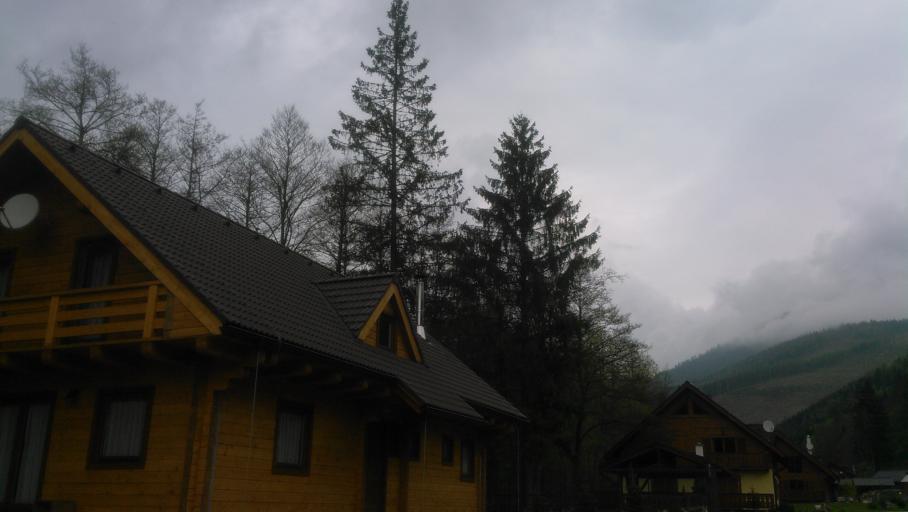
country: SK
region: Banskobystricky
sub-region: Okres Banska Bystrica
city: Brezno
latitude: 48.8628
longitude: 19.6046
